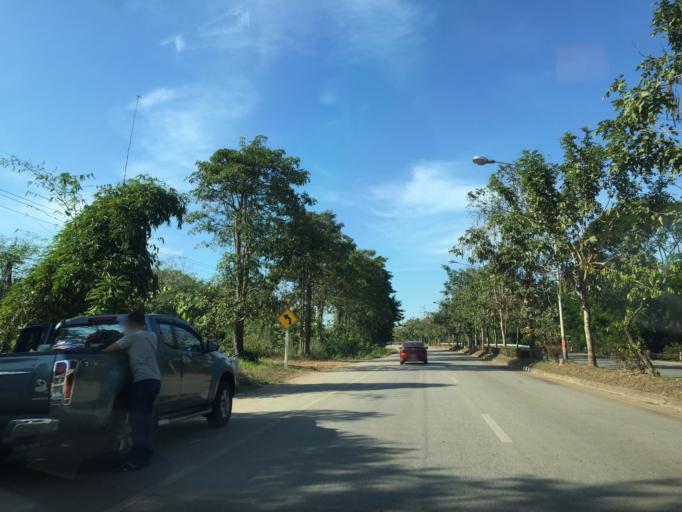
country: TH
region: Loei
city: Wang Saphung
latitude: 17.3142
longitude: 101.7710
